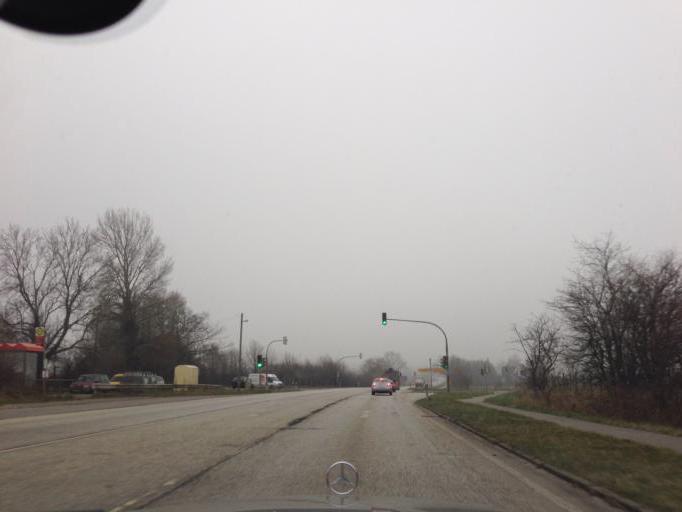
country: DE
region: Schleswig-Holstein
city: Grossbarkau
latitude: 54.2649
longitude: 10.1502
